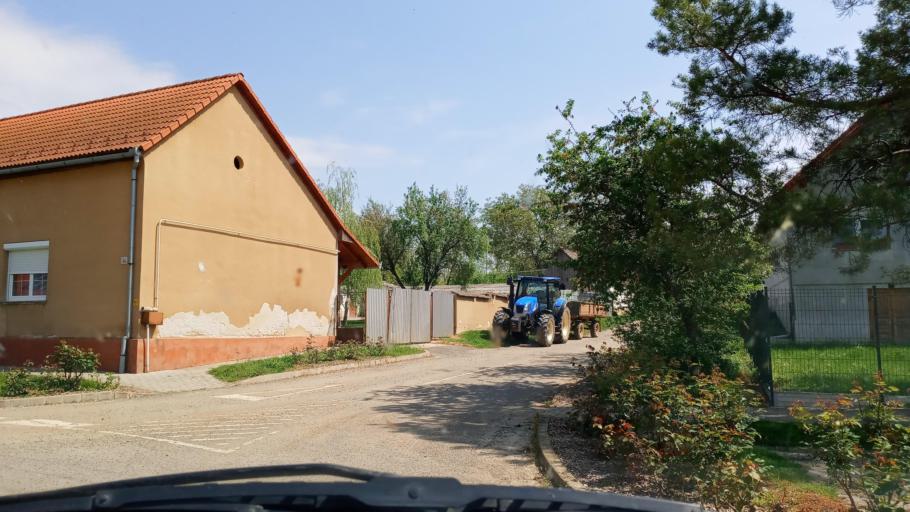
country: HR
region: Osjecko-Baranjska
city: Beli Manastir
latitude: 45.8618
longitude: 18.5861
